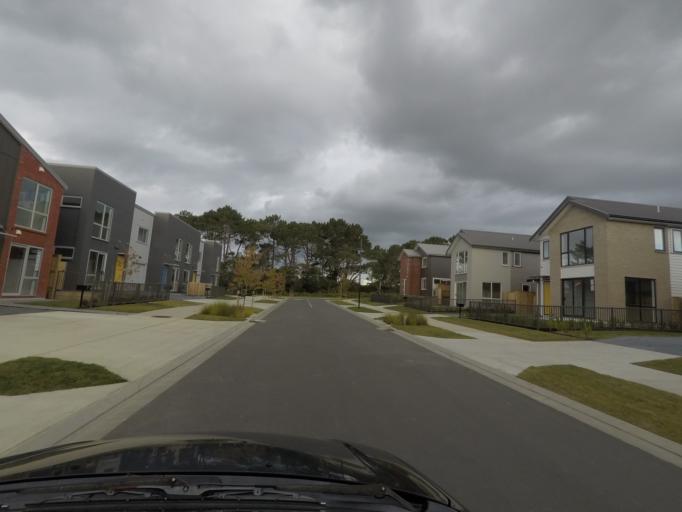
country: NZ
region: Auckland
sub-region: Auckland
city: Rosebank
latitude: -36.8271
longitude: 174.6255
